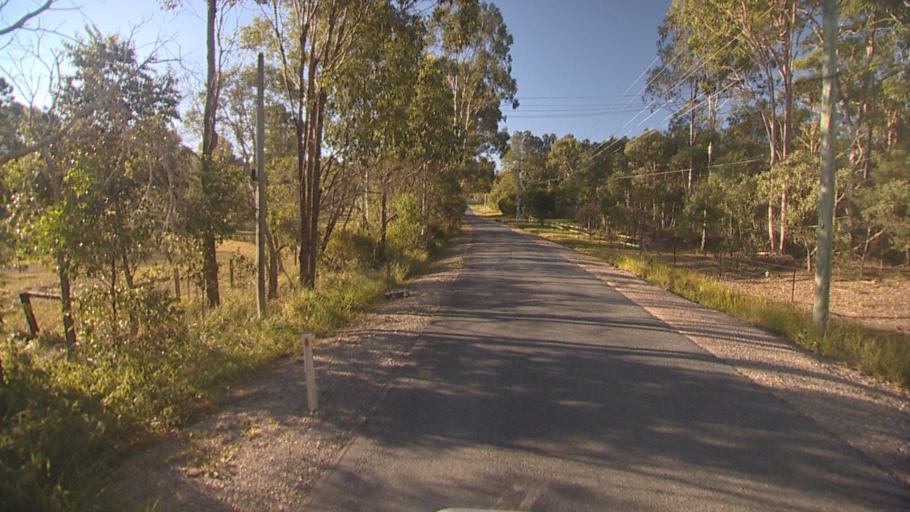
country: AU
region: Queensland
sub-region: Logan
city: Chambers Flat
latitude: -27.7765
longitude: 153.1286
